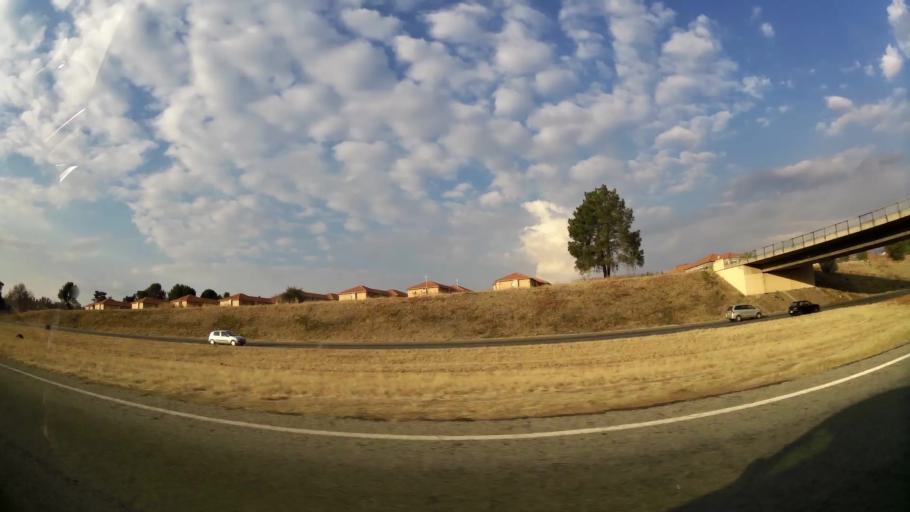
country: ZA
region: Gauteng
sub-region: Sedibeng District Municipality
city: Vanderbijlpark
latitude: -26.7463
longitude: 27.8262
